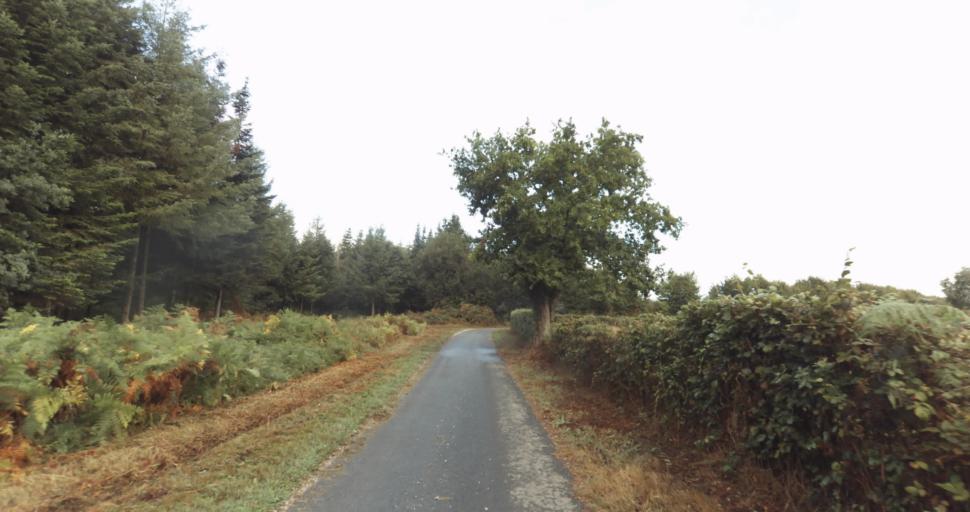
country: FR
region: Lower Normandy
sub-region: Departement de l'Orne
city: Vimoutiers
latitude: 48.8998
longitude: 0.2491
